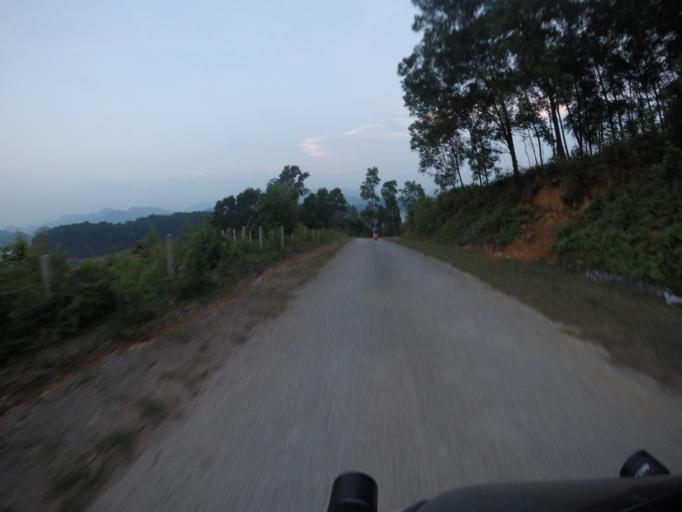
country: VN
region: Thai Nguyen
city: Chua Hang
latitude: 21.5825
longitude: 105.7141
